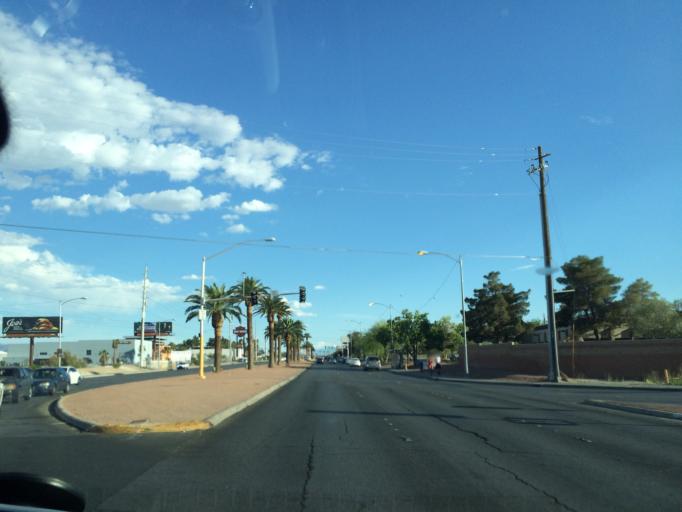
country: US
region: Nevada
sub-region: Clark County
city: Paradise
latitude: 36.0863
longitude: -115.1731
